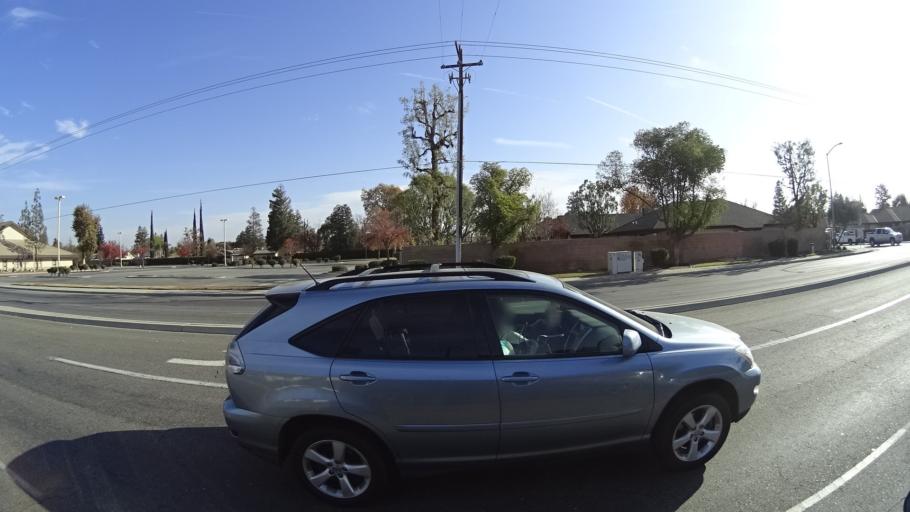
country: US
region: California
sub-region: Kern County
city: Greenacres
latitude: 35.4087
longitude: -119.0745
